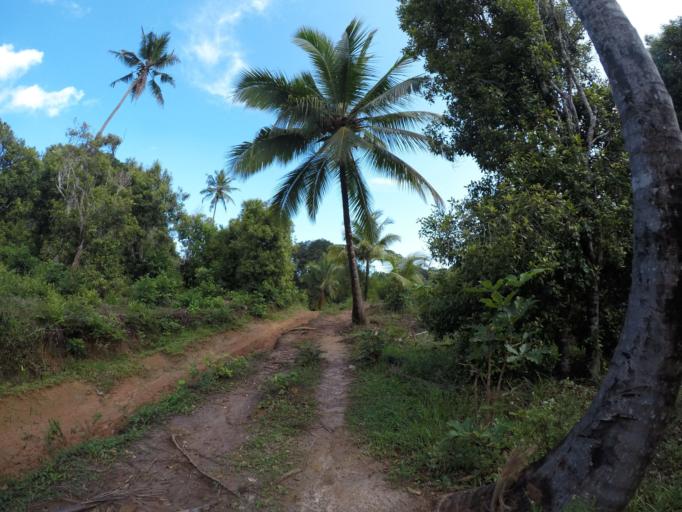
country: TZ
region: Pemba South
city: Mtambile
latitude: -5.3829
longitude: 39.7193
